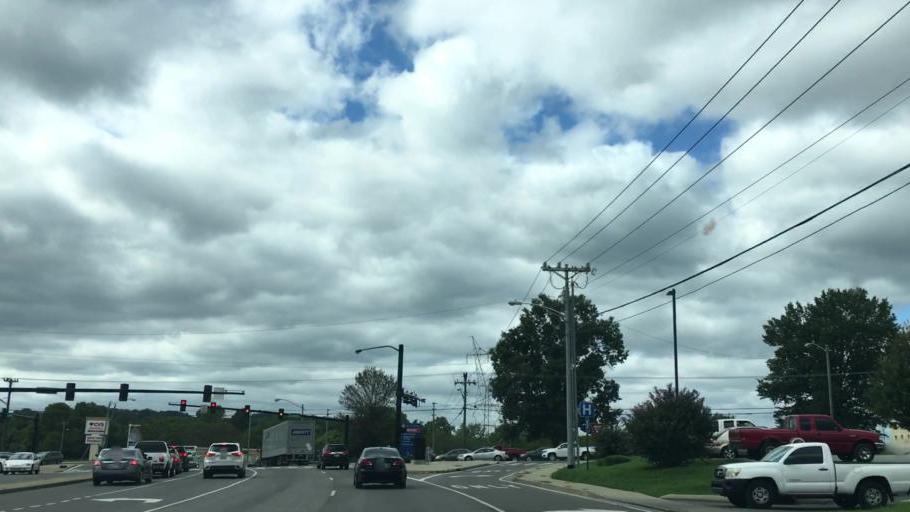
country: US
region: Tennessee
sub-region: Maury County
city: Columbia
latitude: 35.6043
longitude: -87.0666
